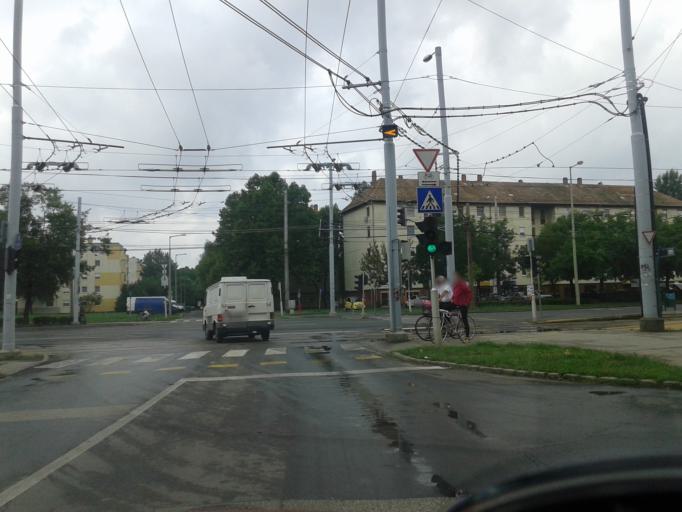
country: HU
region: Csongrad
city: Szeged
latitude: 46.2725
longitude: 20.1437
